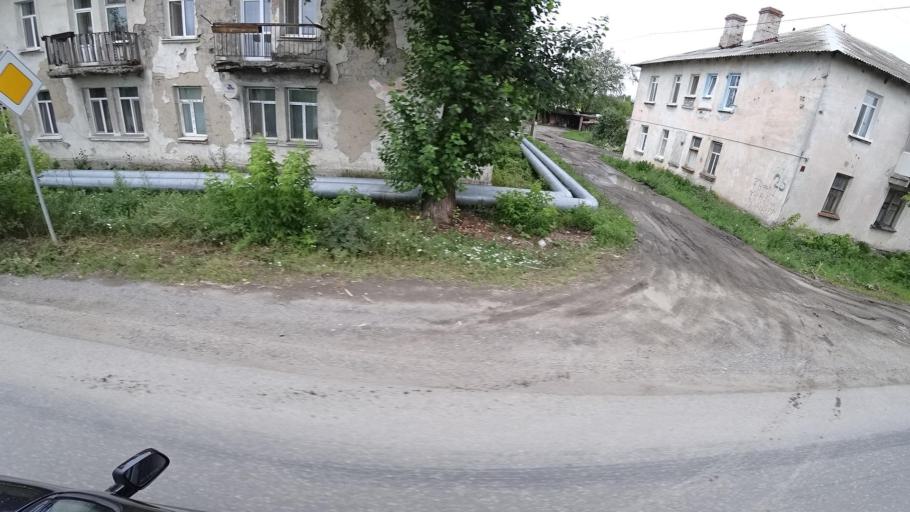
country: RU
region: Sverdlovsk
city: Kamyshlov
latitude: 56.8418
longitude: 62.7240
